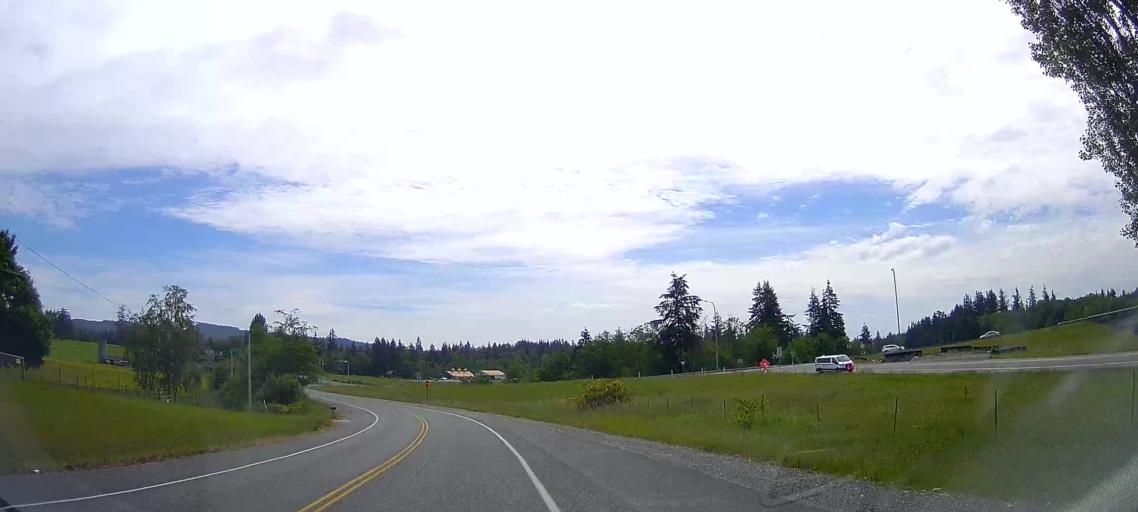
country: US
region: Washington
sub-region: Snohomish County
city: Stanwood
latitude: 48.3105
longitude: -122.3166
